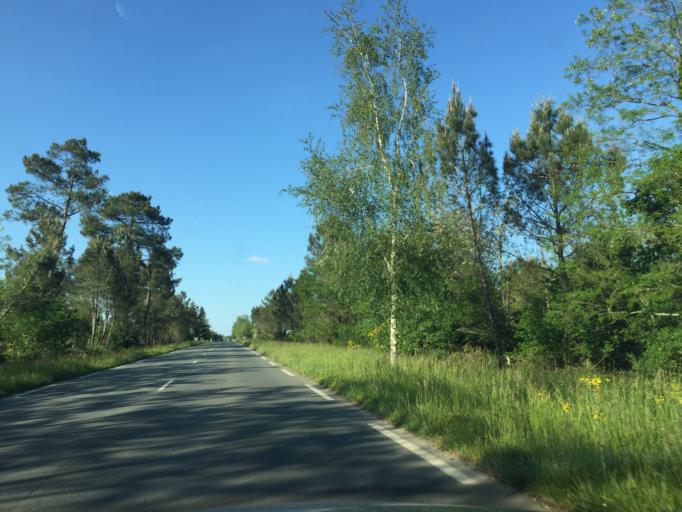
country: FR
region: Aquitaine
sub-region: Departement de la Dordogne
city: La Roche-Chalais
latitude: 45.1700
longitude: 0.0149
